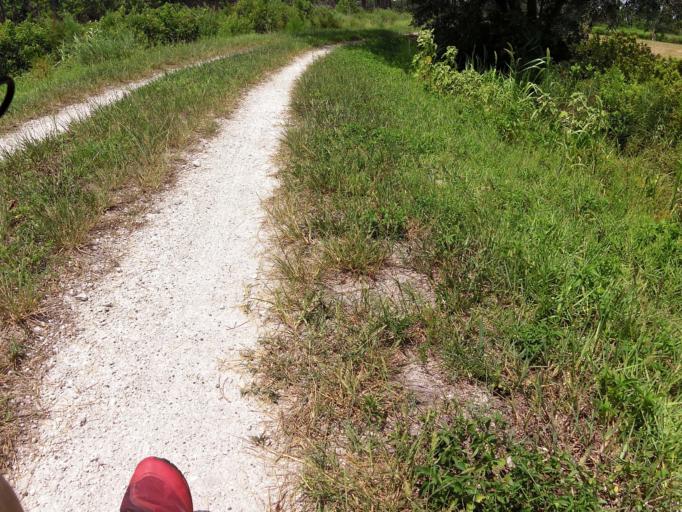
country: US
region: Florida
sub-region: Saint Johns County
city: Villano Beach
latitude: 30.0359
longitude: -81.3420
